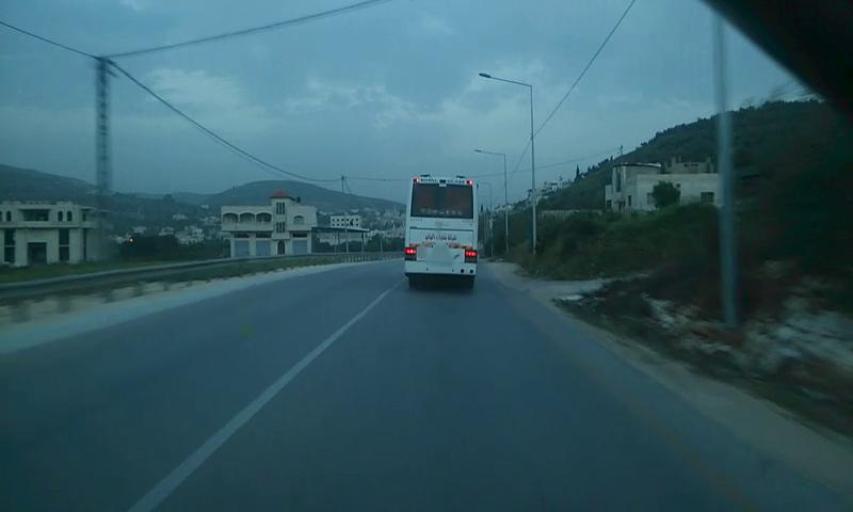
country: PS
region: West Bank
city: Kafr al Labad
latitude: 32.3111
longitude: 35.1036
